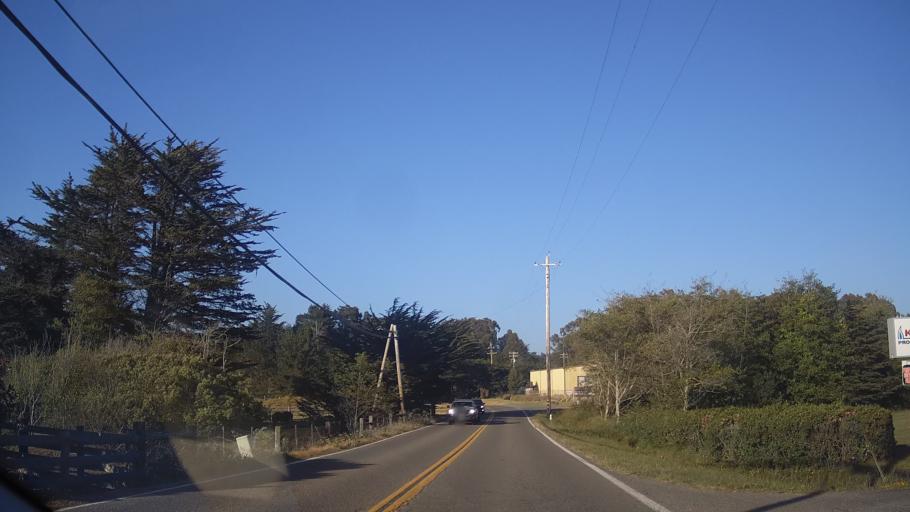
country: US
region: California
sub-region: Mendocino County
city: Fort Bragg
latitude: 39.4695
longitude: -123.8011
